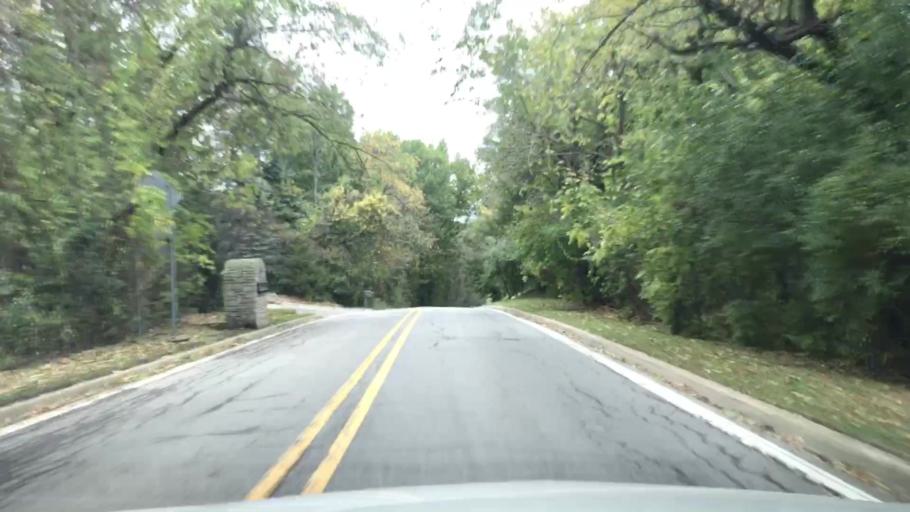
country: US
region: Michigan
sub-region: Oakland County
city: Rochester
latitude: 42.7422
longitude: -83.1214
